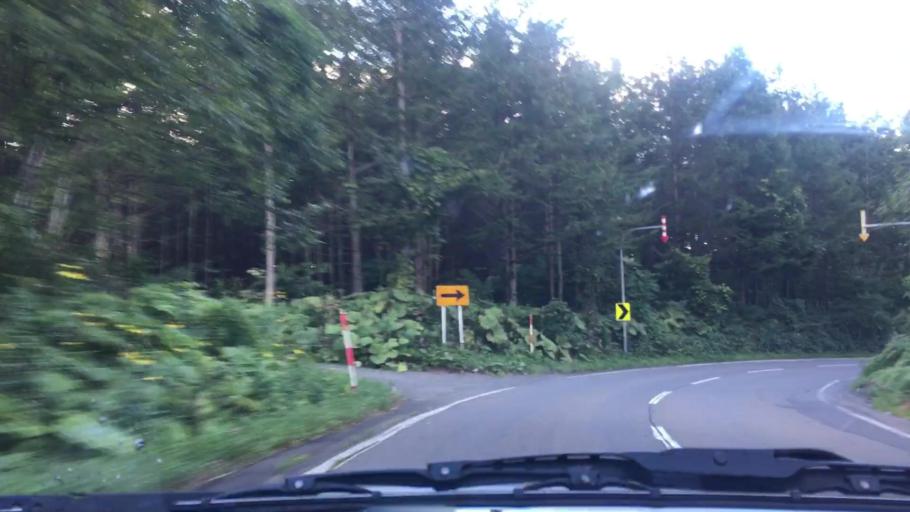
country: JP
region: Hokkaido
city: Otofuke
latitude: 43.1760
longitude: 142.9258
